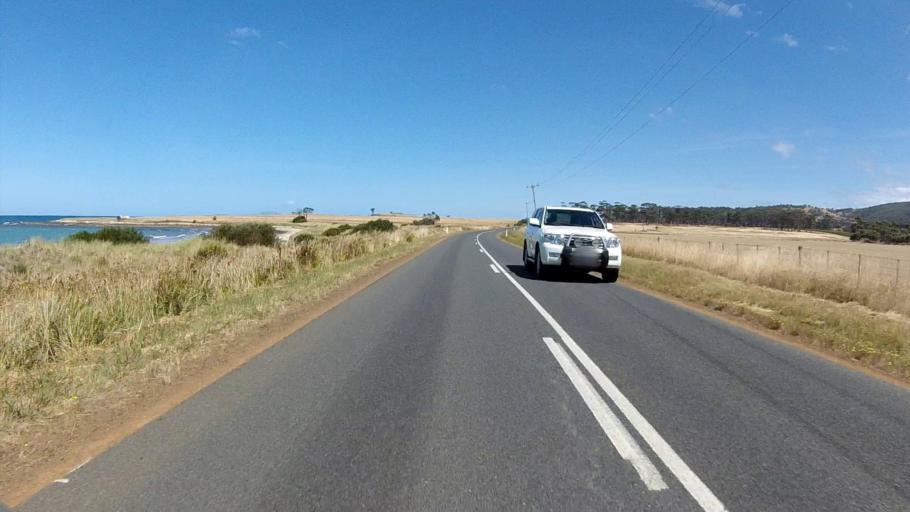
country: AU
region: Tasmania
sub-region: Sorell
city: Sorell
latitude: -42.2032
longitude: 148.0432
